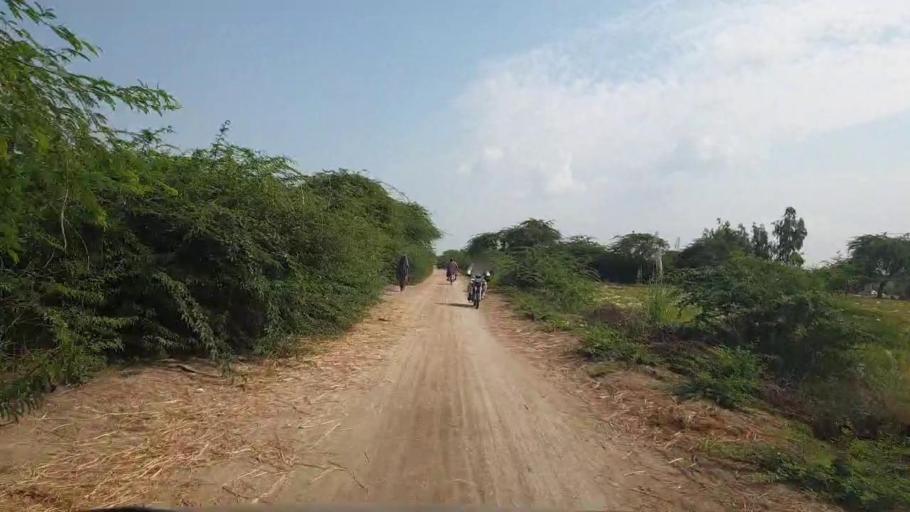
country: PK
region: Sindh
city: Badin
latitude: 24.4658
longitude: 68.5814
